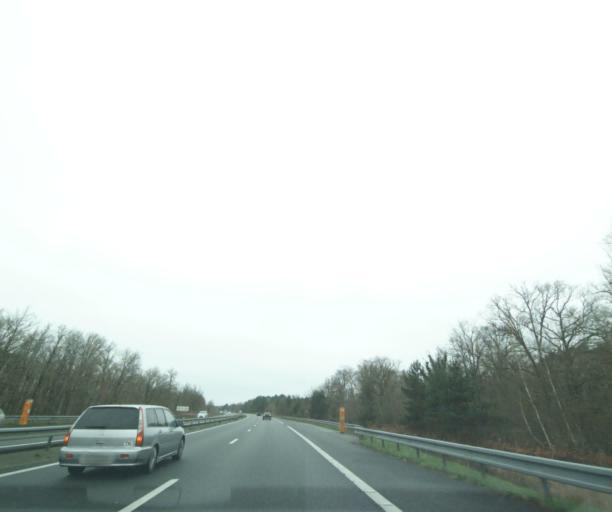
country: FR
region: Centre
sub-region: Departement du Loir-et-Cher
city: Nouan-le-Fuzelier
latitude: 47.5273
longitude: 2.0034
